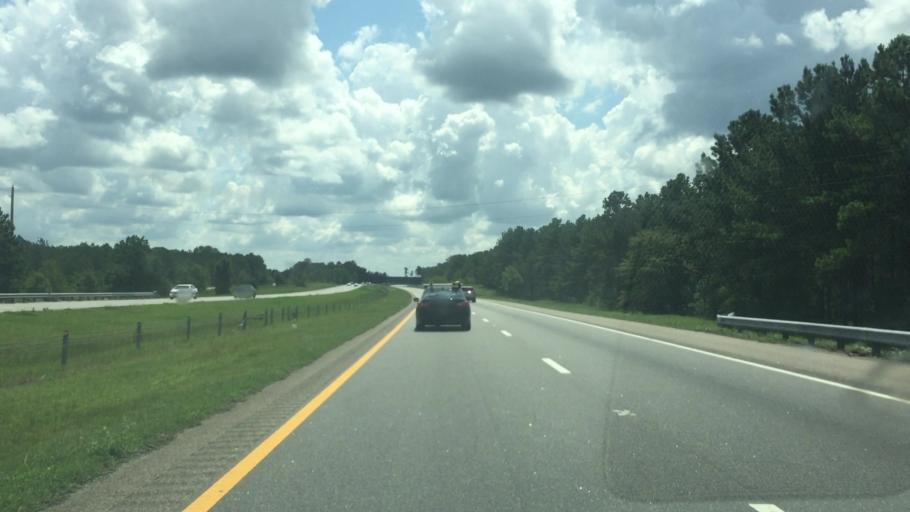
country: US
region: North Carolina
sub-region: Richmond County
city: East Rockingham
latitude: 34.8730
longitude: -79.7652
